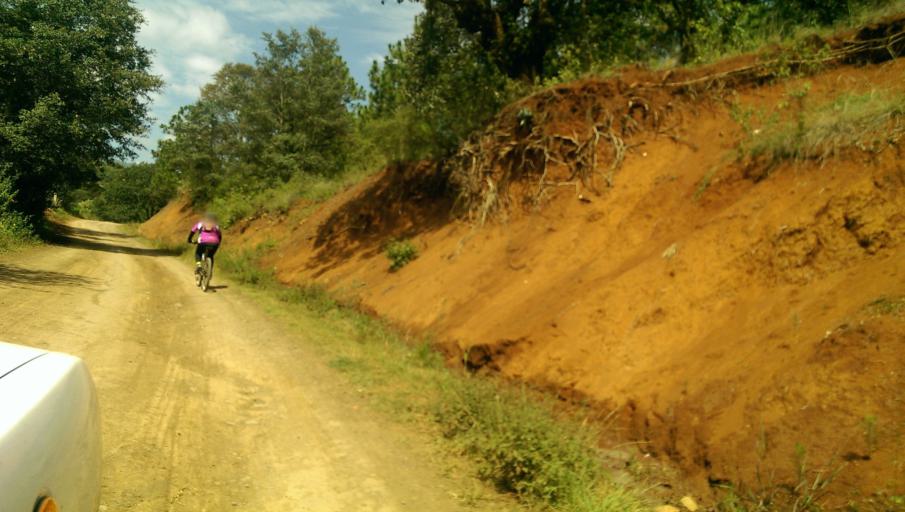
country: MX
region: Michoacan
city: Acuitzio del Canje
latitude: 19.4715
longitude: -101.3662
